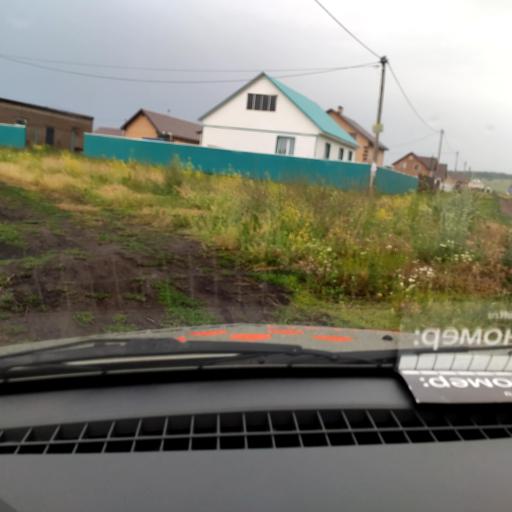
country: RU
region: Bashkortostan
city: Mikhaylovka
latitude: 54.8632
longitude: 55.7394
